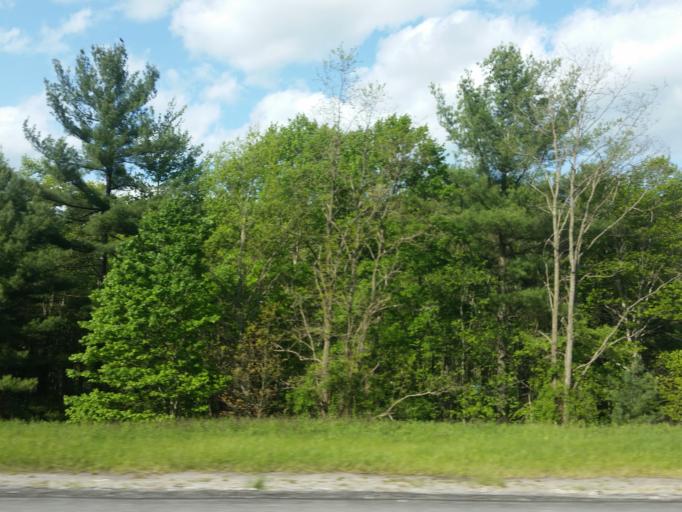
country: US
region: West Virginia
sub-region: Raleigh County
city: Shady Spring
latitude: 37.6794
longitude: -81.1231
